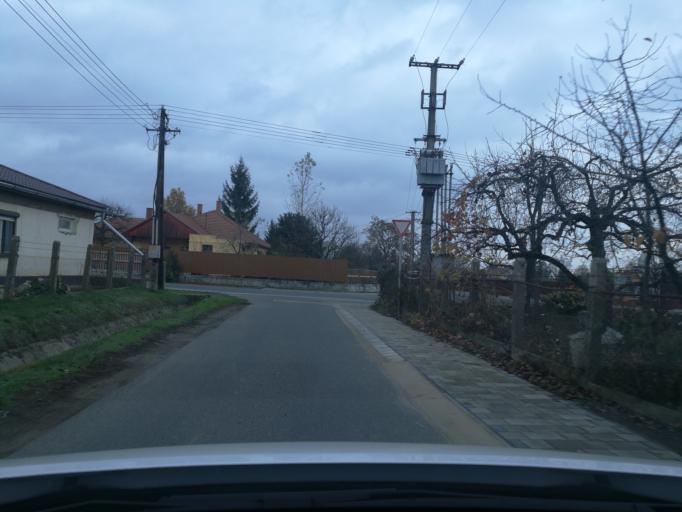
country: HU
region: Szabolcs-Szatmar-Bereg
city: Nyirpazony
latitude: 47.9801
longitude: 21.7945
